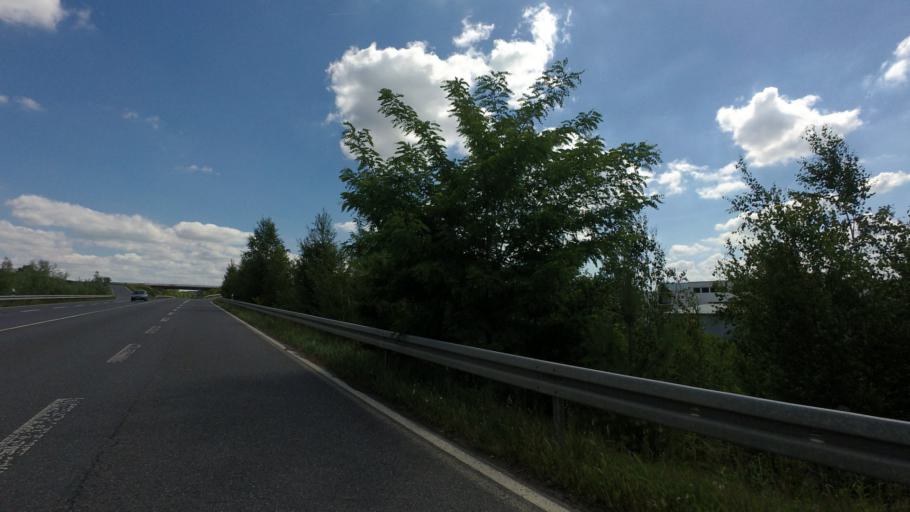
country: DE
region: Brandenburg
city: Senftenberg
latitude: 51.5290
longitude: 14.0134
